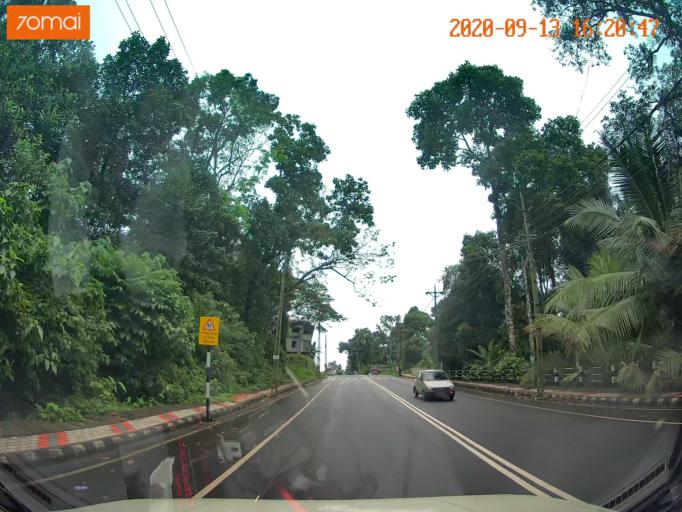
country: IN
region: Kerala
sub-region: Kottayam
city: Lalam
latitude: 9.7052
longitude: 76.6632
